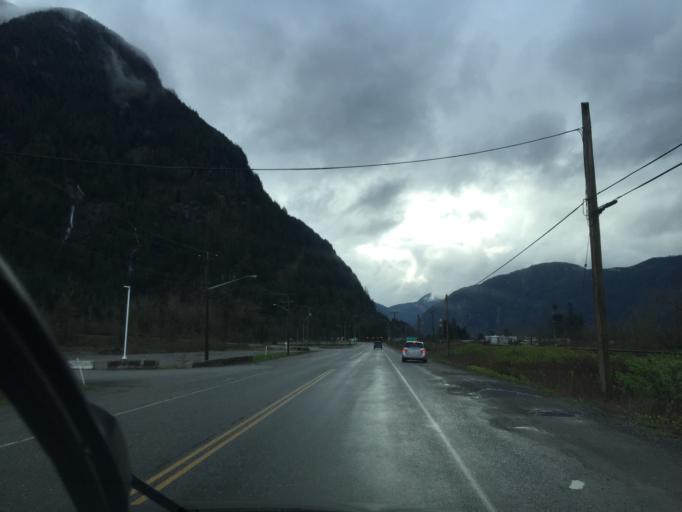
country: CA
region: British Columbia
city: Hope
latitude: 49.3657
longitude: -121.5172
